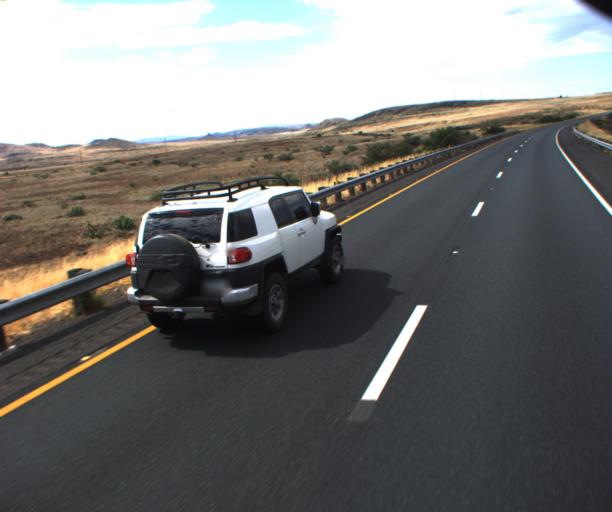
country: US
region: Arizona
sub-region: Yavapai County
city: Cordes Lakes
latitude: 34.4481
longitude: -112.0357
